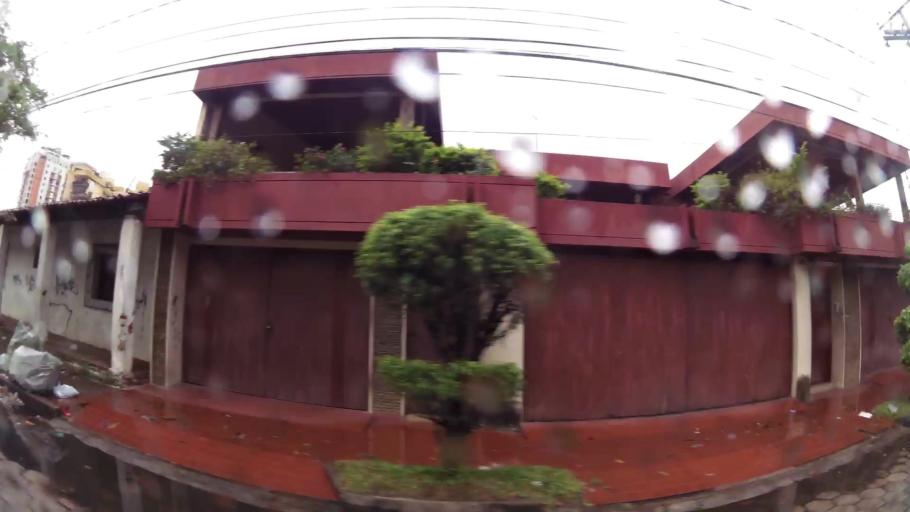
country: BO
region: Santa Cruz
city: Santa Cruz de la Sierra
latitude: -17.7754
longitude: -63.1686
